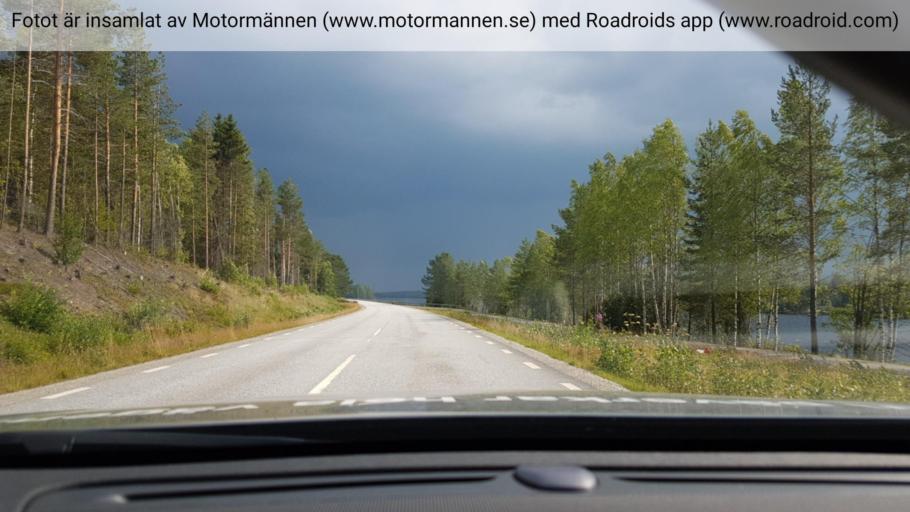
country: SE
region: Vaesterbotten
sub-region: Vindelns Kommun
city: Vindeln
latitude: 64.1794
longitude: 19.4779
